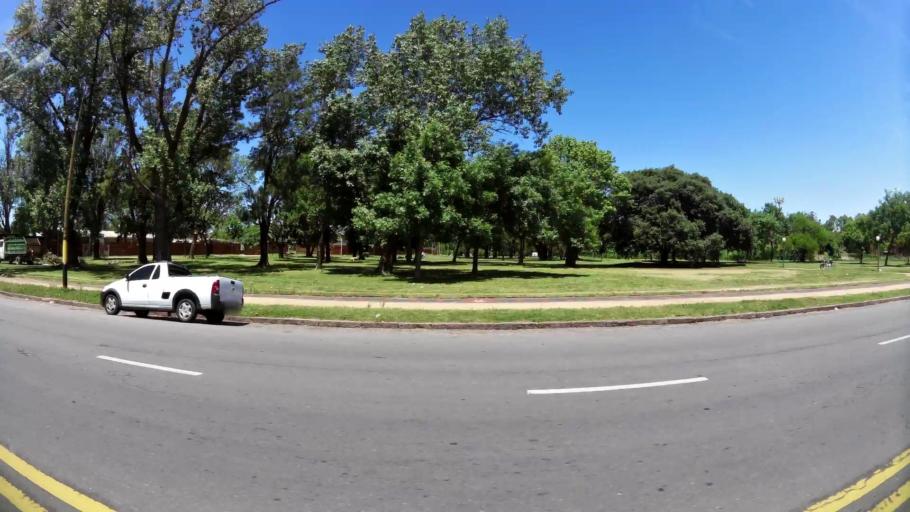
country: UY
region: Montevideo
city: Montevideo
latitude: -34.8965
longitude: -56.1550
